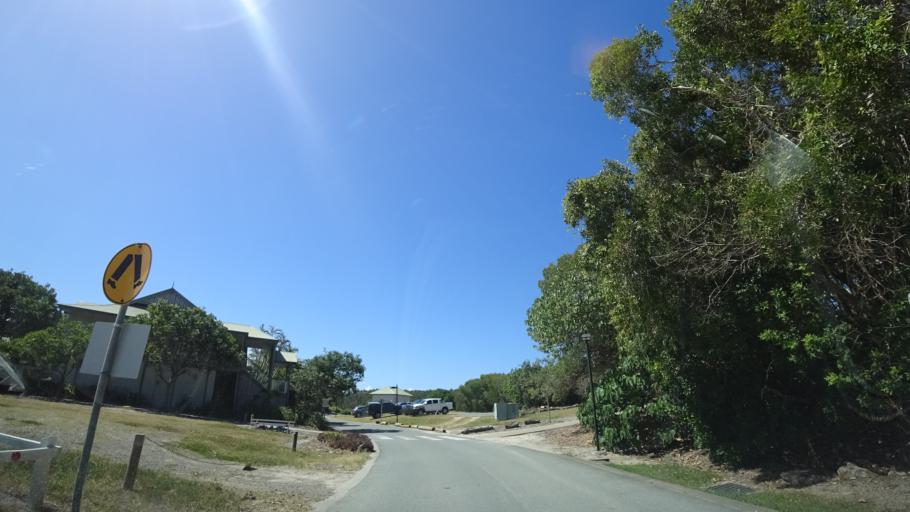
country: AU
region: Queensland
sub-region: Sunshine Coast
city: Mooloolaba
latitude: -26.6326
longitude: 153.1001
